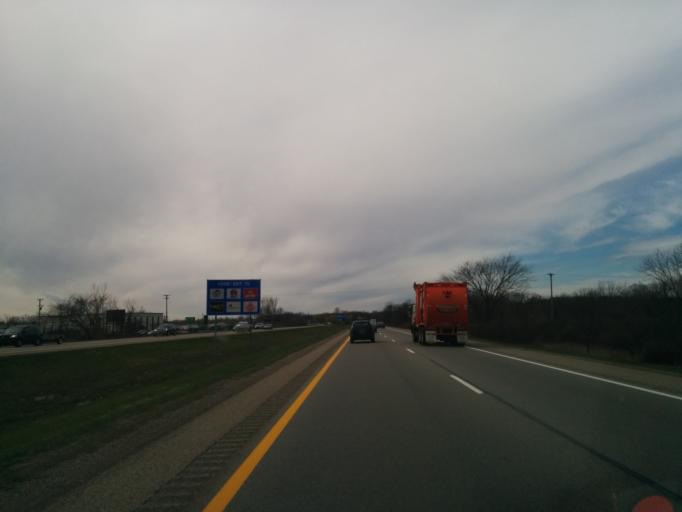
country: US
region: Michigan
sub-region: Kent County
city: Grandville
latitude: 42.9237
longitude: -85.7525
